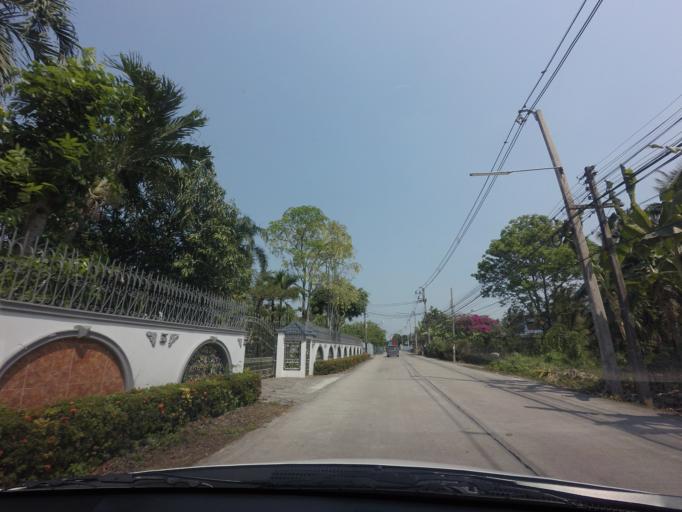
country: TH
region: Nakhon Pathom
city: Sam Phran
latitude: 13.7625
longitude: 100.2548
